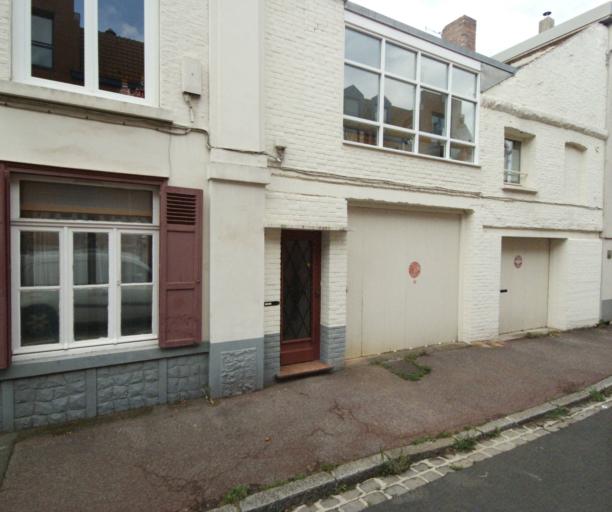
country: FR
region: Nord-Pas-de-Calais
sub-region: Departement du Nord
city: Lille
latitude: 50.6468
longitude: 3.0547
